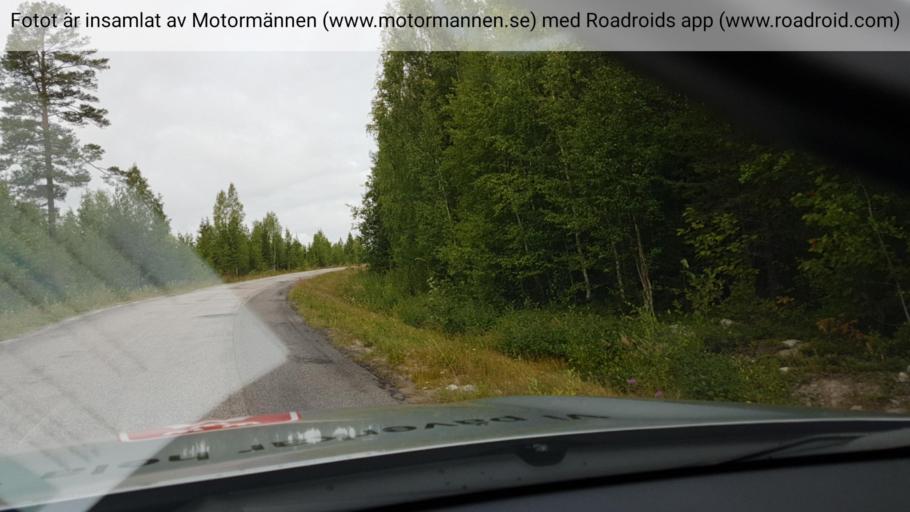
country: SE
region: Norrbotten
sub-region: Bodens Kommun
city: Saevast
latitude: 65.6673
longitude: 21.7235
